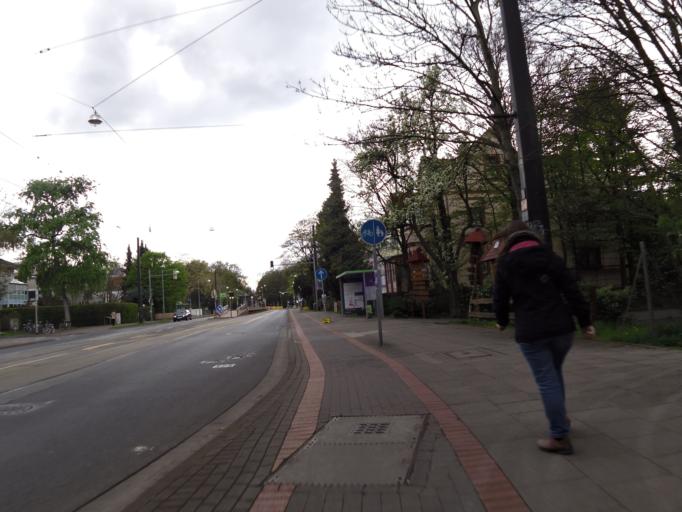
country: DE
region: Lower Saxony
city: Laatzen
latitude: 52.3648
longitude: 9.8142
